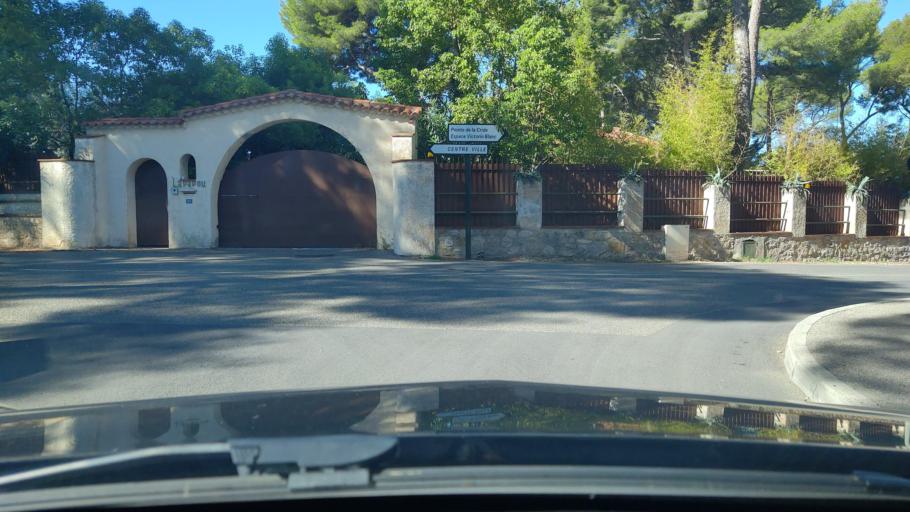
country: FR
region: Provence-Alpes-Cote d'Azur
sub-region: Departement du Var
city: Sanary-sur-Mer
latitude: 43.1188
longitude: 5.7817
